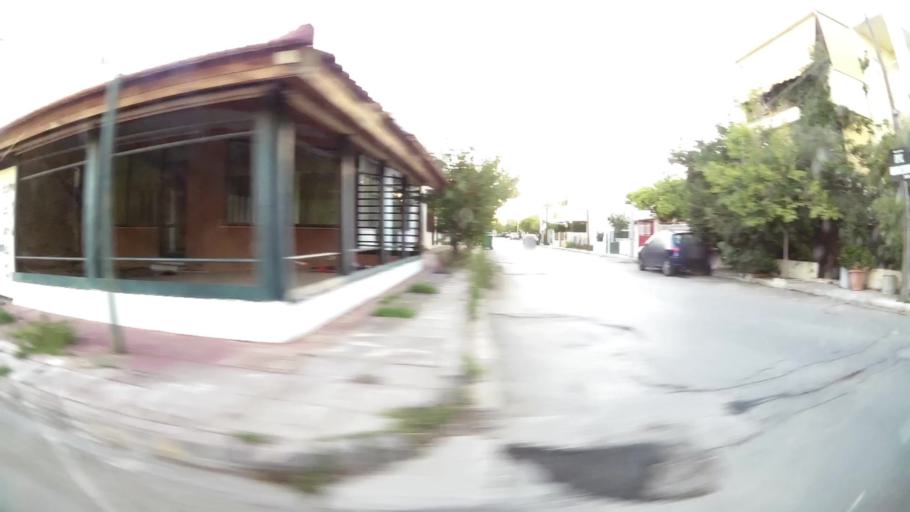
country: GR
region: Attica
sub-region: Nomarchia Dytikis Attikis
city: Ano Liosia
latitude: 38.0852
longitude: 23.6991
